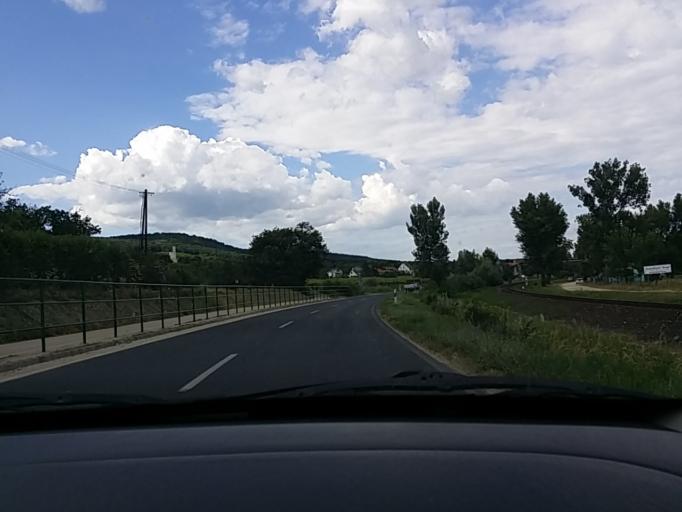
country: HU
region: Veszprem
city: Revfueloep
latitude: 46.8360
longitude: 17.6461
